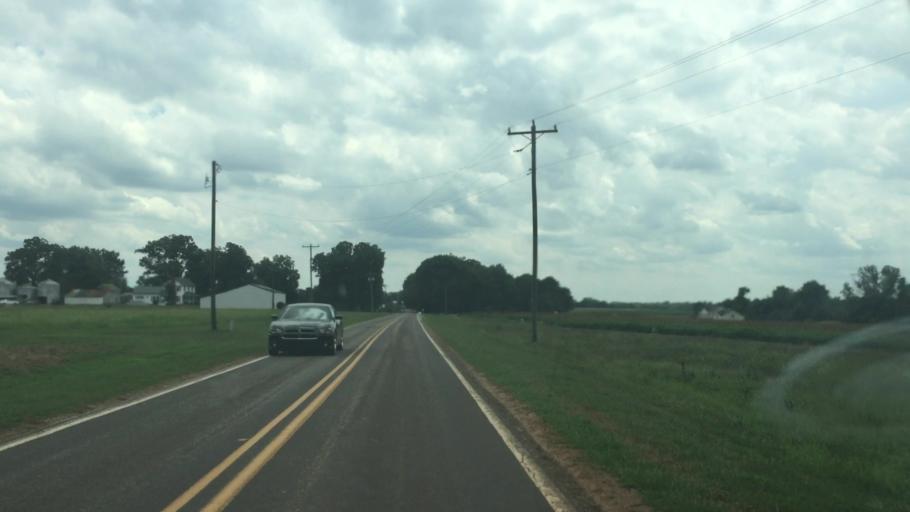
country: US
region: North Carolina
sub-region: Rowan County
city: Landis
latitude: 35.6436
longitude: -80.6683
